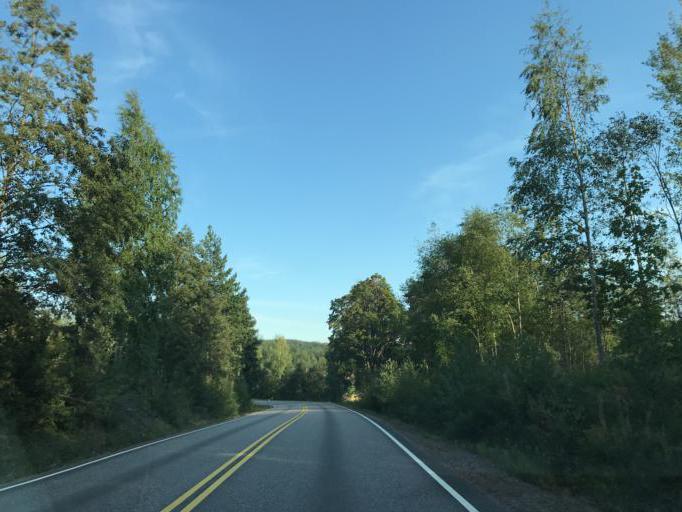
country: FI
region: Uusimaa
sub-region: Helsinki
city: Vihti
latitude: 60.4175
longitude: 24.3893
